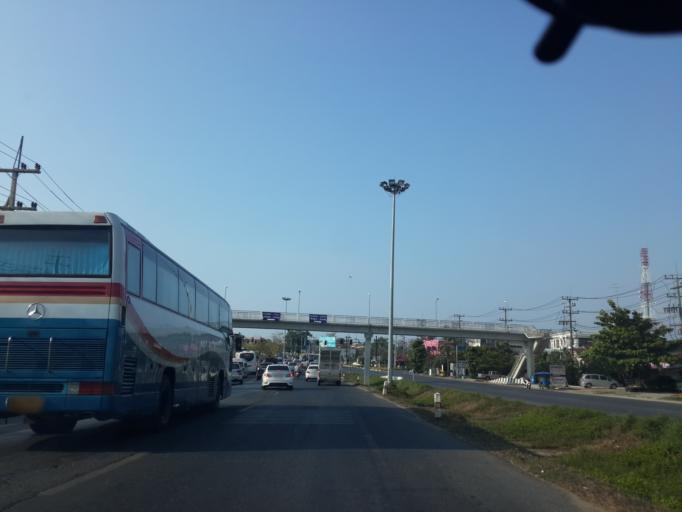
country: TH
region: Chon Buri
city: Phatthaya
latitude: 12.8558
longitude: 100.9091
